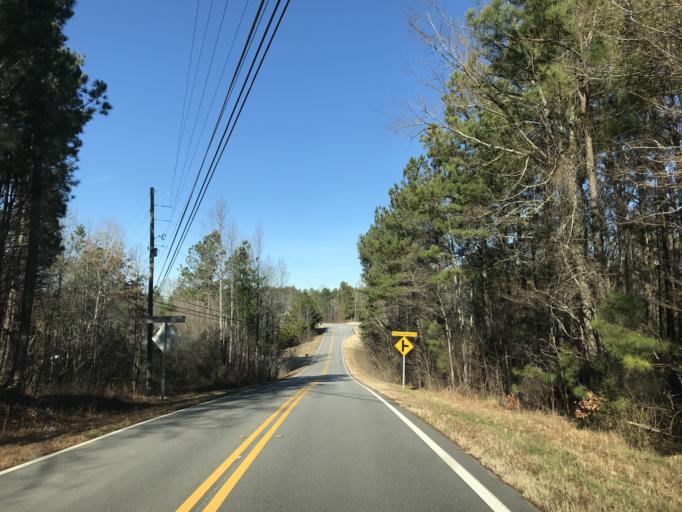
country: US
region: Georgia
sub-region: Paulding County
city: Dallas
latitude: 33.9836
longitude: -84.8862
